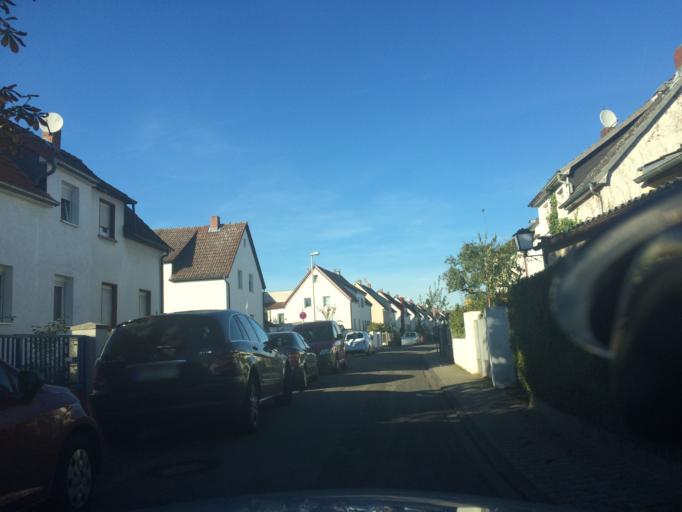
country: DE
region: Hesse
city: Morfelden-Walldorf
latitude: 49.9796
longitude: 8.5709
